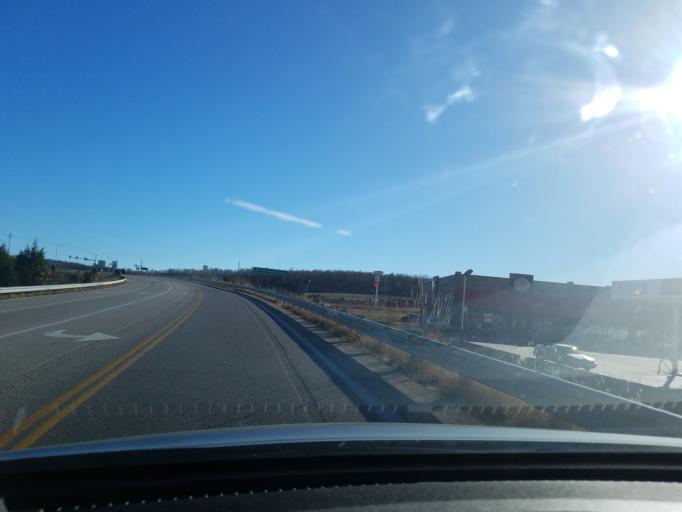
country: US
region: Missouri
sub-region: Pulaski County
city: Waynesville
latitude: 37.8076
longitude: -92.2235
